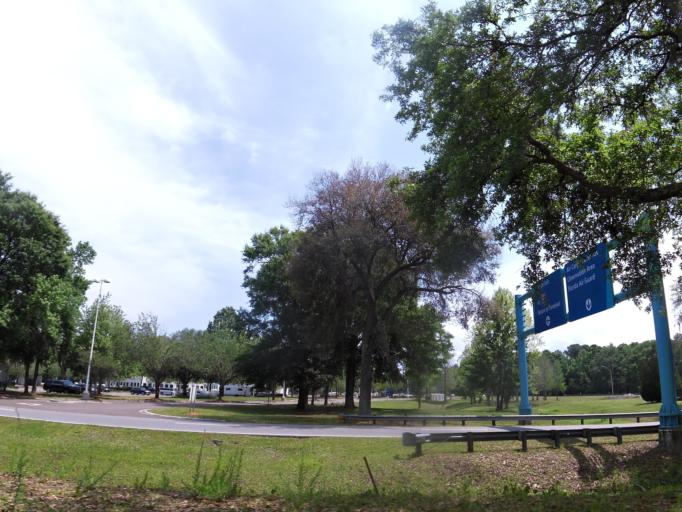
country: US
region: Florida
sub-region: Nassau County
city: Nassau Village-Ratliff
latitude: 30.4900
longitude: -81.6756
